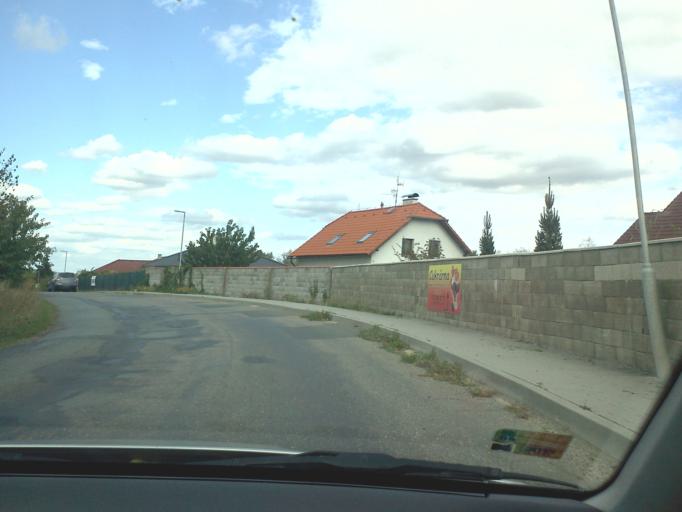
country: CZ
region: Central Bohemia
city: Mukarov
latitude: 50.0190
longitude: 14.7876
